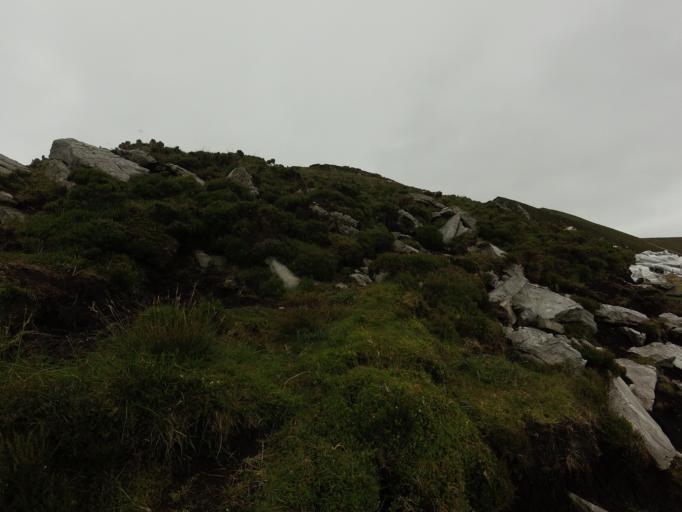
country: IE
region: Ulster
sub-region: County Donegal
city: Killybegs
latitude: 54.6429
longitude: -8.6853
